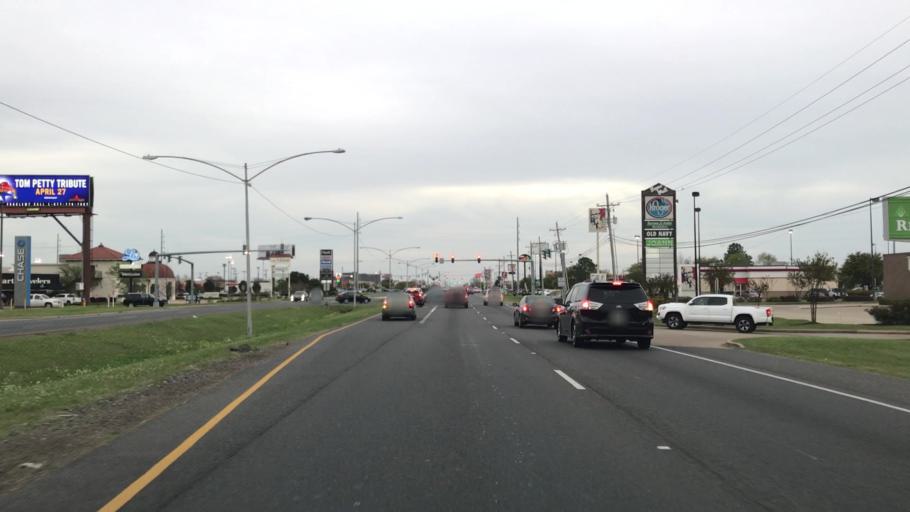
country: US
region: Louisiana
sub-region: Bossier Parish
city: Bossier City
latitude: 32.4465
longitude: -93.7205
